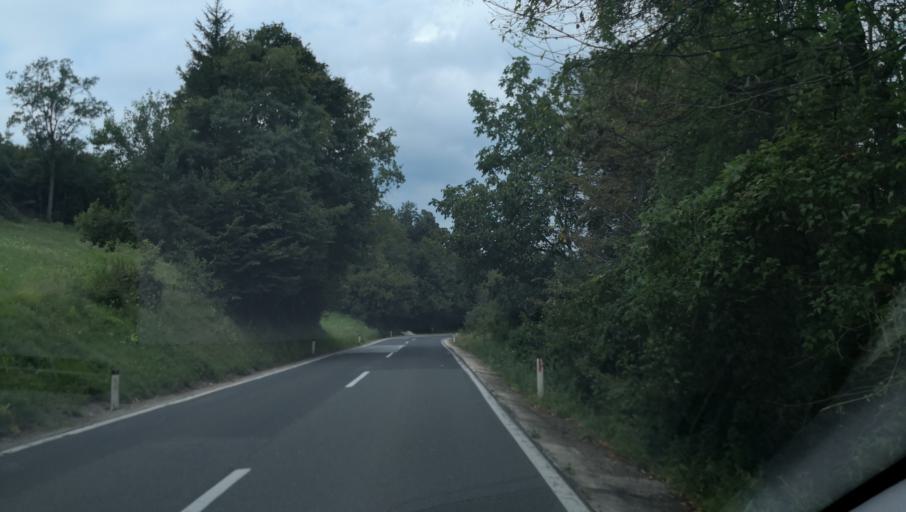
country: SI
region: Novo Mesto
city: Novo Mesto
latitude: 45.7448
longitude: 15.2094
